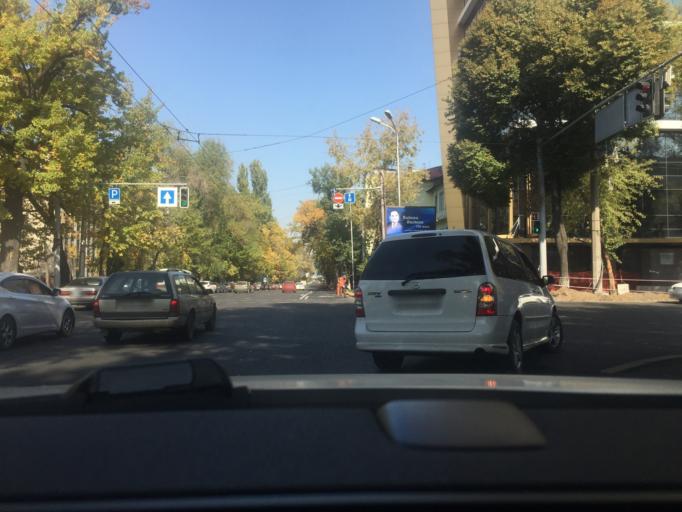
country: KZ
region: Almaty Qalasy
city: Almaty
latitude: 43.2633
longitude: 76.9387
